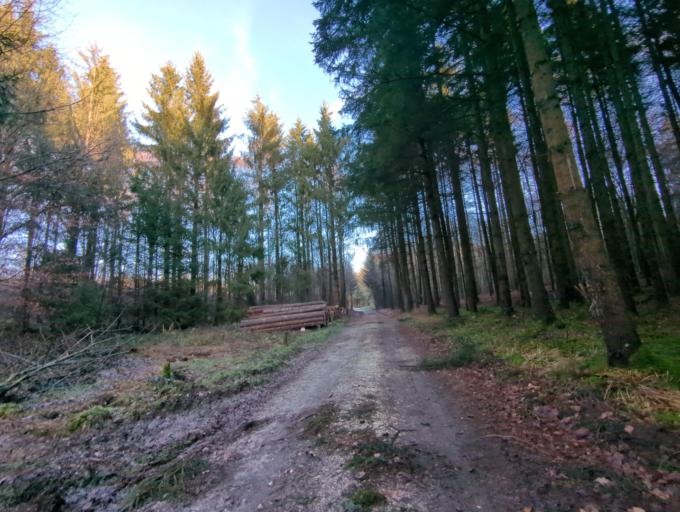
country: DE
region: Bavaria
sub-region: Swabia
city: Wasserburg
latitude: 48.4287
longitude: 10.3090
